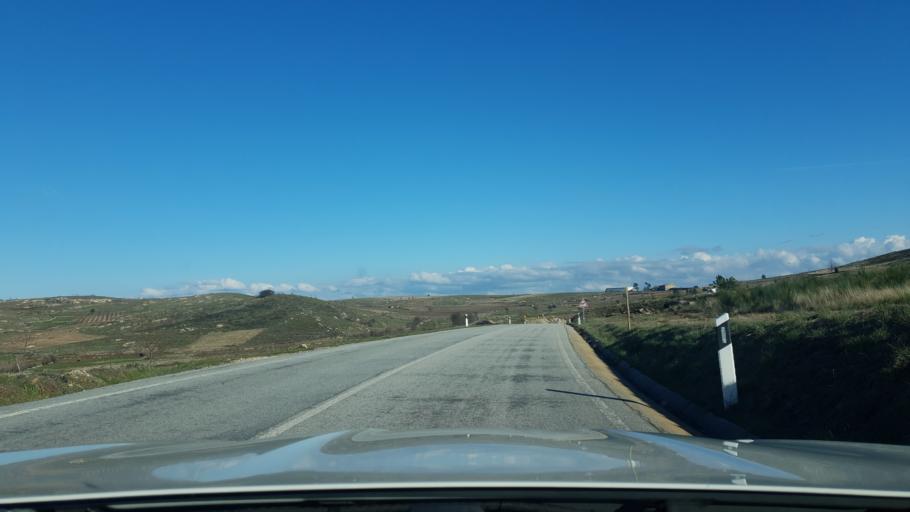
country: PT
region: Braganca
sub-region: Freixo de Espada A Cinta
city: Freixo de Espada a Cinta
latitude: 41.1813
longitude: -6.8053
